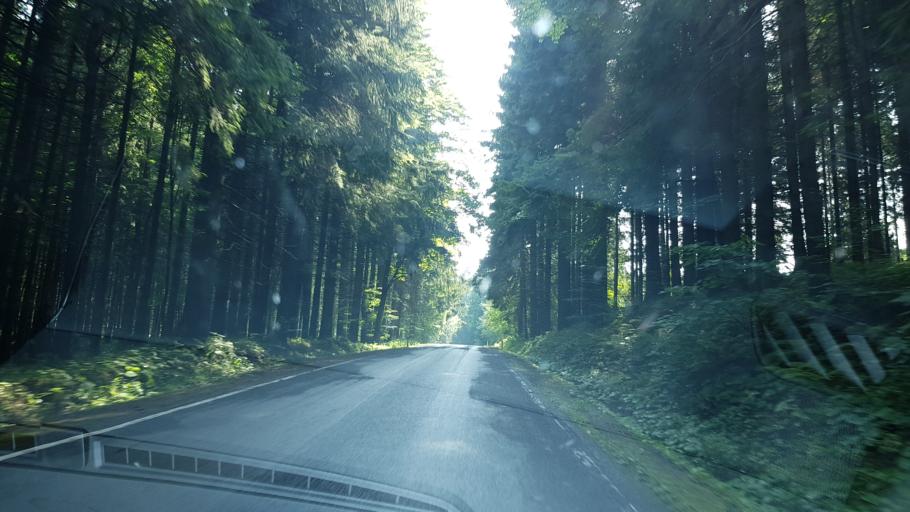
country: CZ
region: Olomoucky
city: Ceska Ves
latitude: 50.2197
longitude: 17.2638
